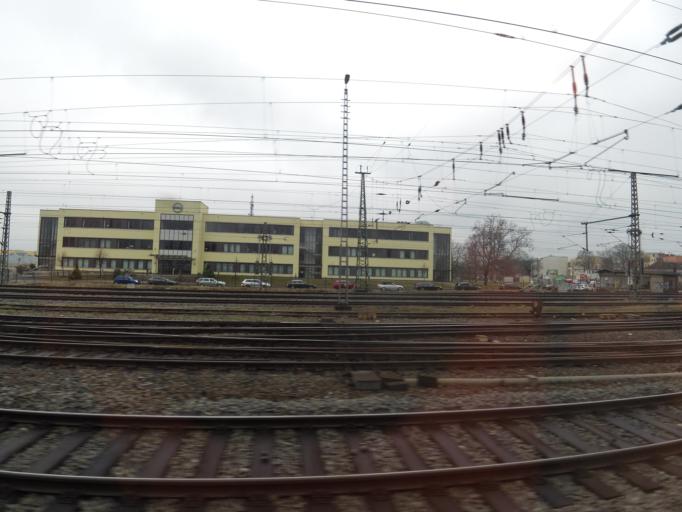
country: DE
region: Saxony-Anhalt
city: Halle (Saale)
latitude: 51.4729
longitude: 11.9918
